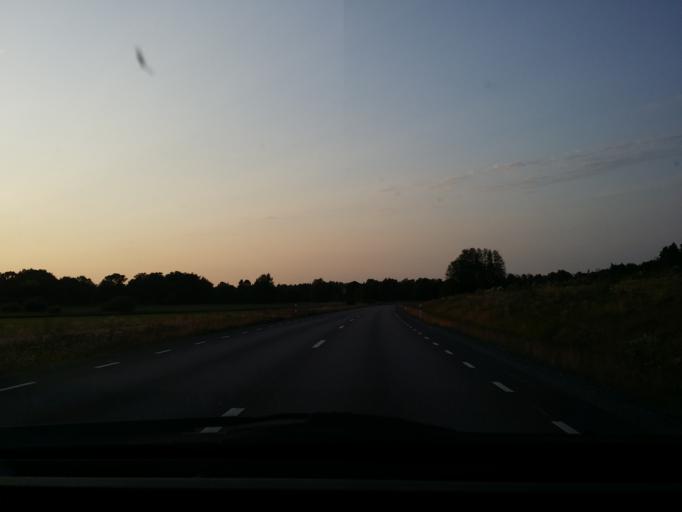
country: SE
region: Vaestmanland
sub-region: Vasteras
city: Tillberga
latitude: 59.5940
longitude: 16.6653
